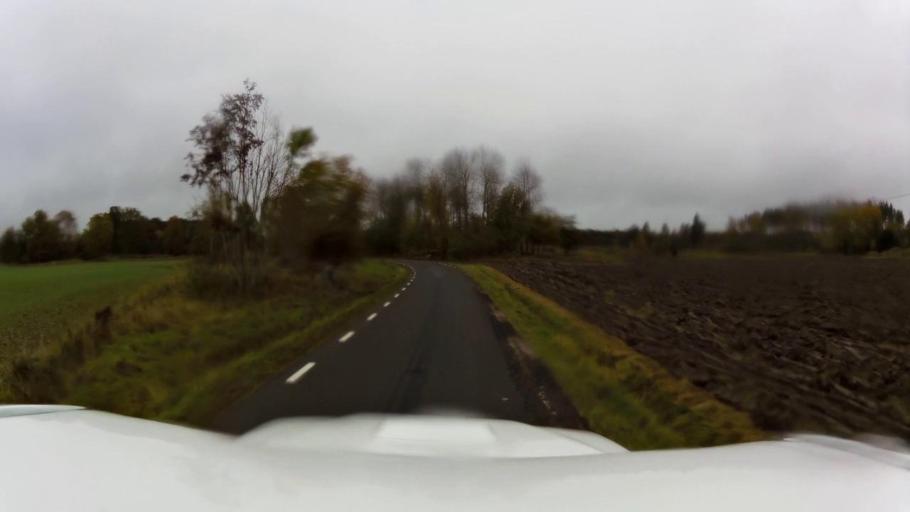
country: SE
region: OEstergoetland
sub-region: Linkopings Kommun
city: Linghem
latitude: 58.3488
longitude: 15.8843
